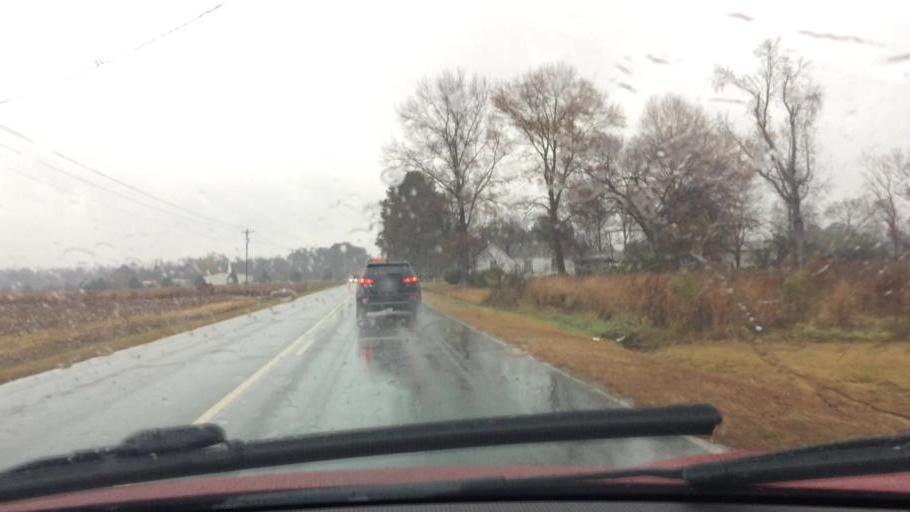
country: US
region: North Carolina
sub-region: Wayne County
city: Elroy
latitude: 35.4069
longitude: -77.9284
